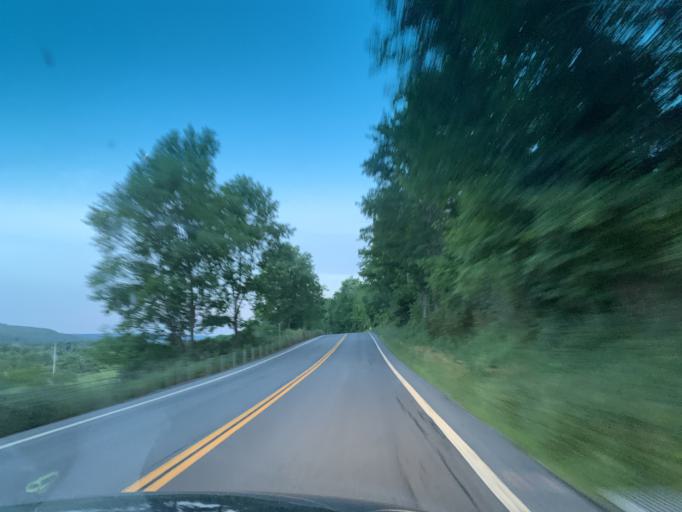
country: US
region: New York
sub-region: Chenango County
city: New Berlin
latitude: 42.6731
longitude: -75.3321
